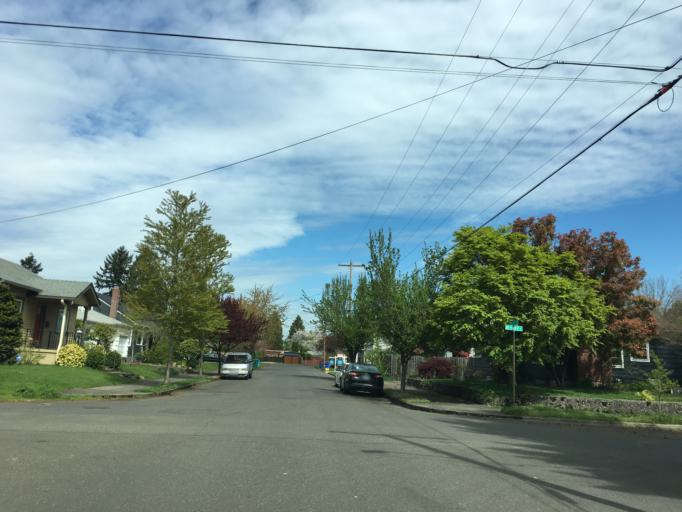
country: US
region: Oregon
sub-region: Multnomah County
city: Lents
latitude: 45.5291
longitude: -122.5914
